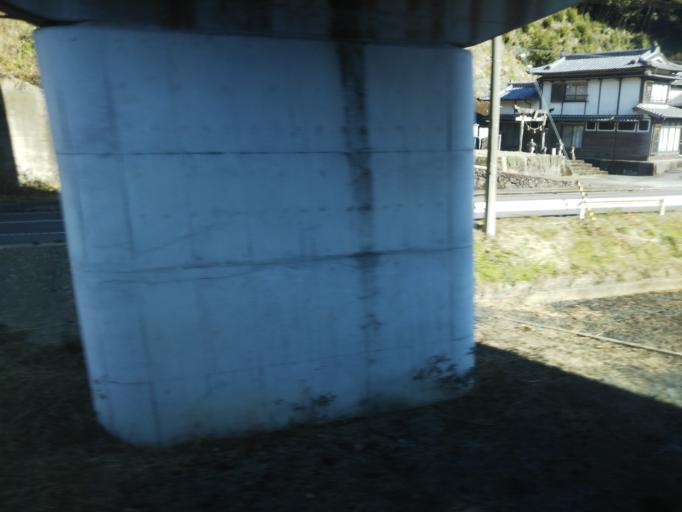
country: JP
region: Kochi
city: Nakamura
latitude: 33.1024
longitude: 133.0987
